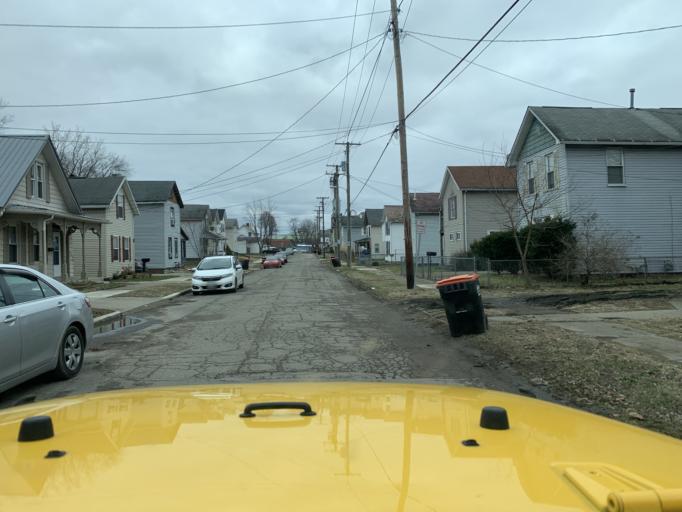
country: US
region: Ohio
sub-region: Licking County
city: Newark
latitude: 40.0546
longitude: -82.4105
